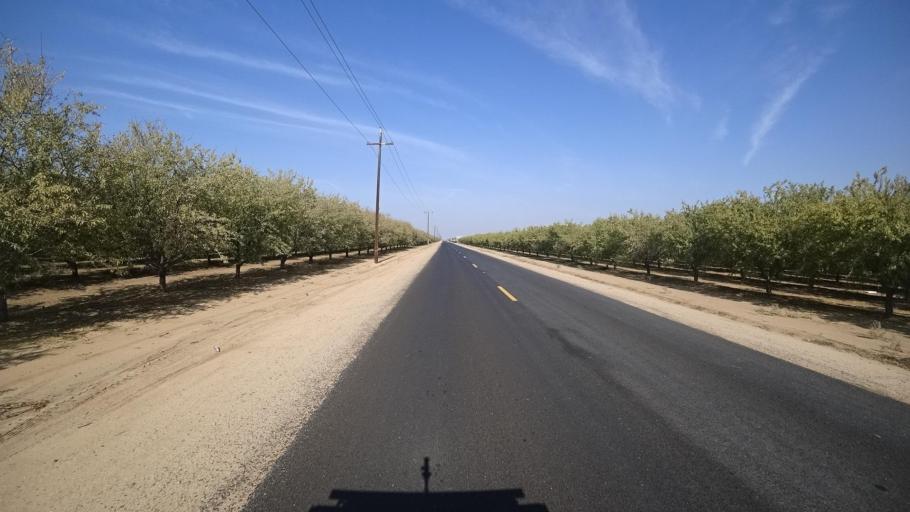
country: US
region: California
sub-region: Kern County
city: Shafter
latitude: 35.5150
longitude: -119.1520
